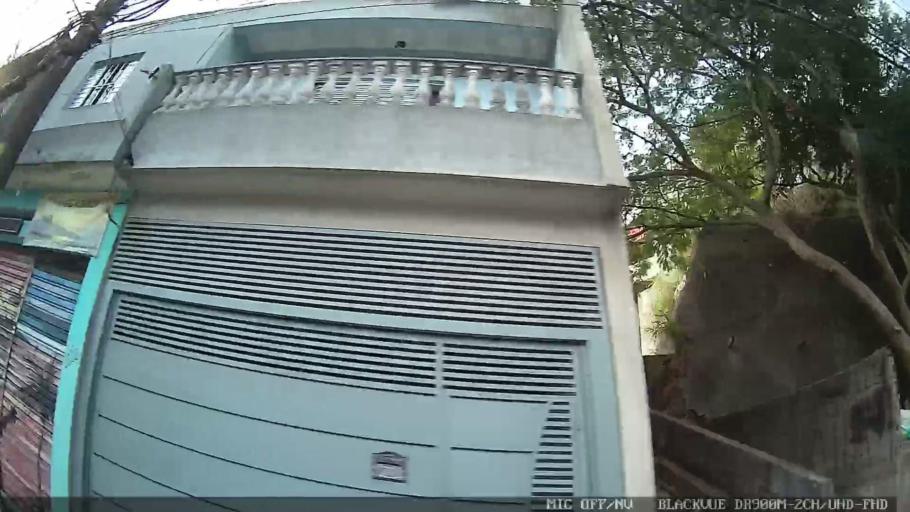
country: BR
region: Sao Paulo
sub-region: Sao Caetano Do Sul
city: Sao Caetano do Sul
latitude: -23.5722
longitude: -46.4916
